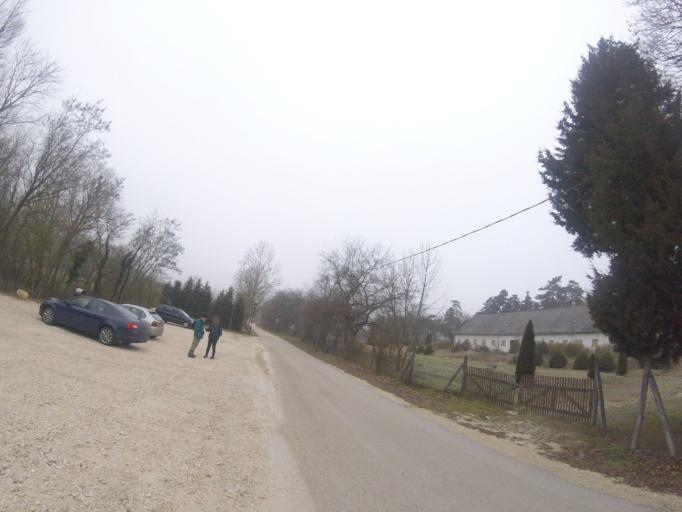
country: HU
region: Fejer
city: Bicske
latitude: 47.4220
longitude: 18.5865
